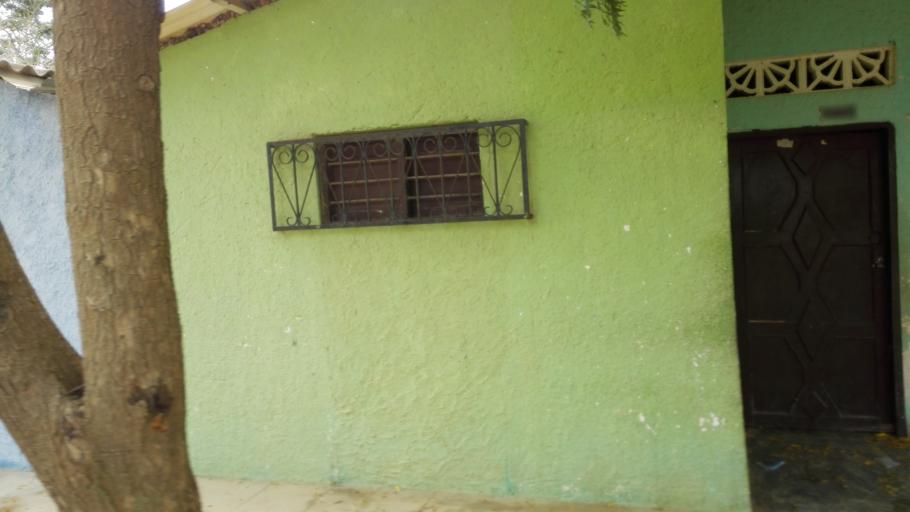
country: CO
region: La Guajira
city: Manaure
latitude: 11.7731
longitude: -72.4454
